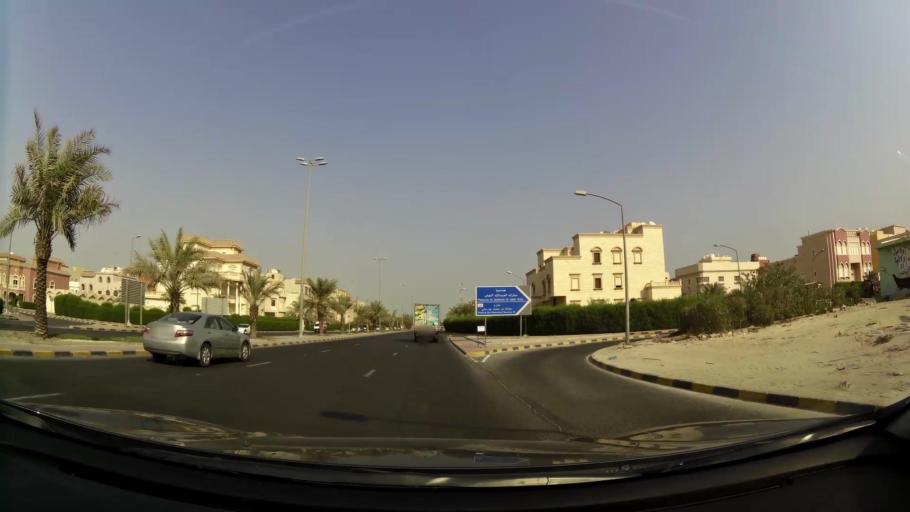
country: KW
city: Bayan
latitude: 29.2842
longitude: 48.0483
